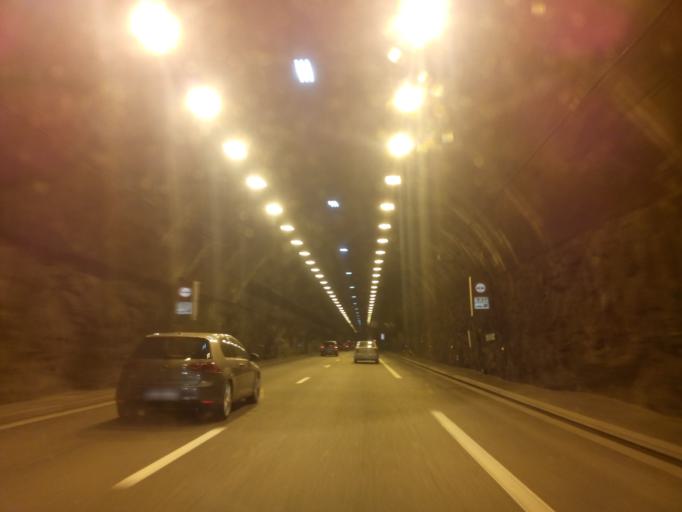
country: FR
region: Rhone-Alpes
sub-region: Departement de la Savoie
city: La Bridoire
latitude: 45.5571
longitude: 5.7331
